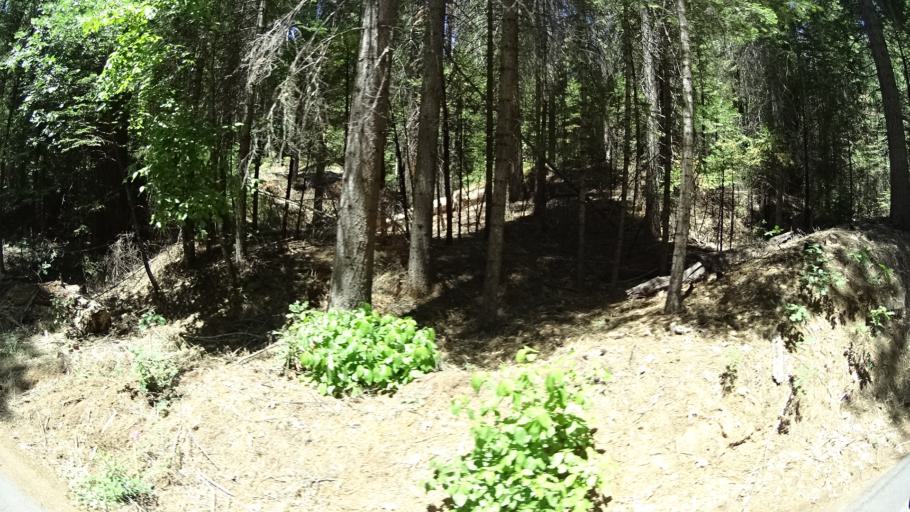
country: US
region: California
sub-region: Calaveras County
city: Arnold
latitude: 38.2317
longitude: -120.3227
